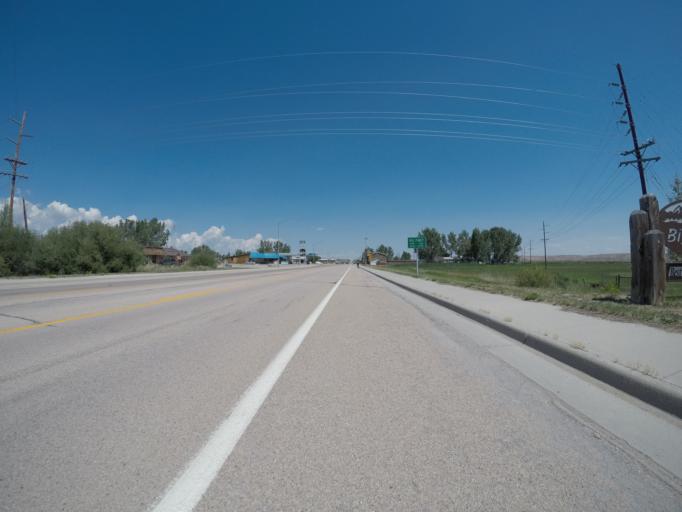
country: US
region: Wyoming
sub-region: Sublette County
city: Marbleton
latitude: 42.5353
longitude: -110.1097
